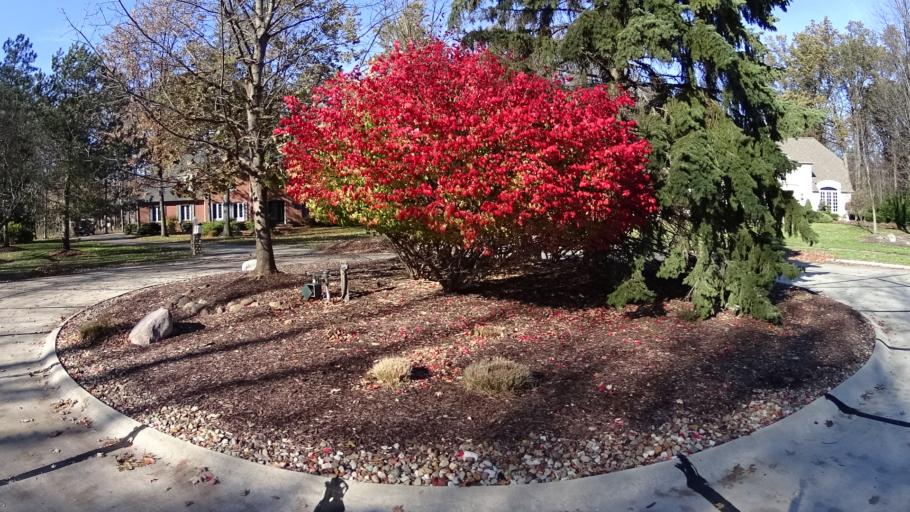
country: US
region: Ohio
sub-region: Lorain County
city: Avon Lake
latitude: 41.4939
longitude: -82.0017
